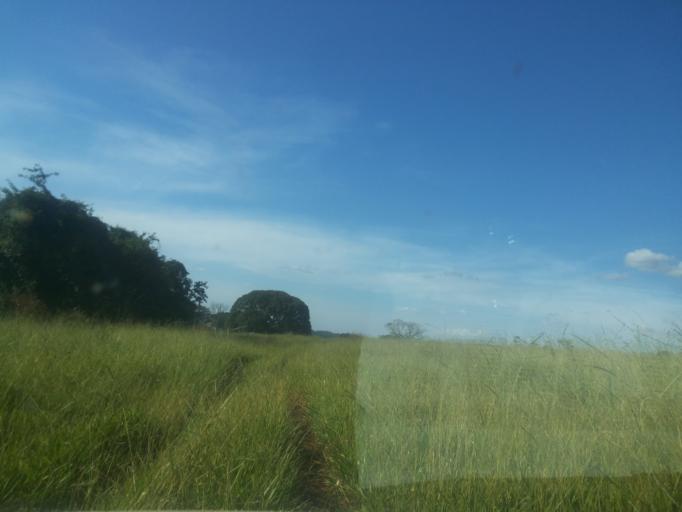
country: BR
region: Minas Gerais
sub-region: Santa Vitoria
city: Santa Vitoria
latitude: -19.0007
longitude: -50.4480
